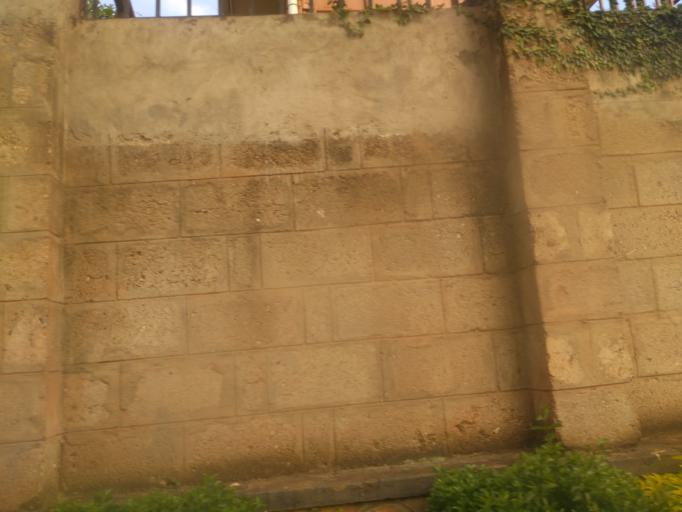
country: UG
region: Central Region
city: Kampala Central Division
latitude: 0.3513
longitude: 32.5946
